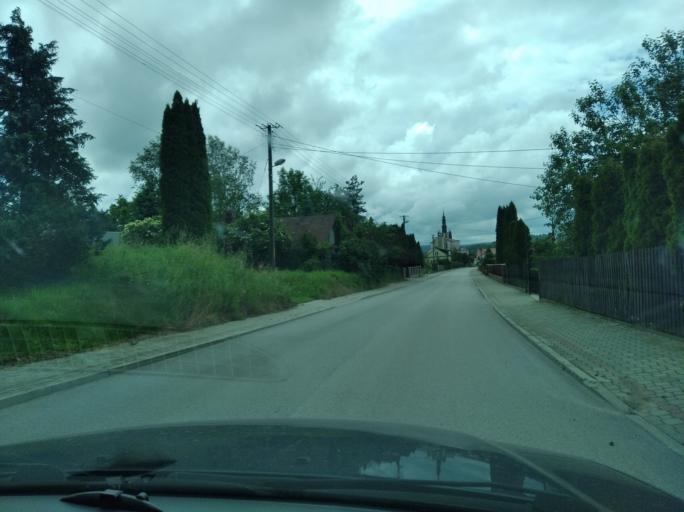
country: PL
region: Subcarpathian Voivodeship
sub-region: Powiat przemyski
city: Dubiecko
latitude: 49.8291
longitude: 22.3939
